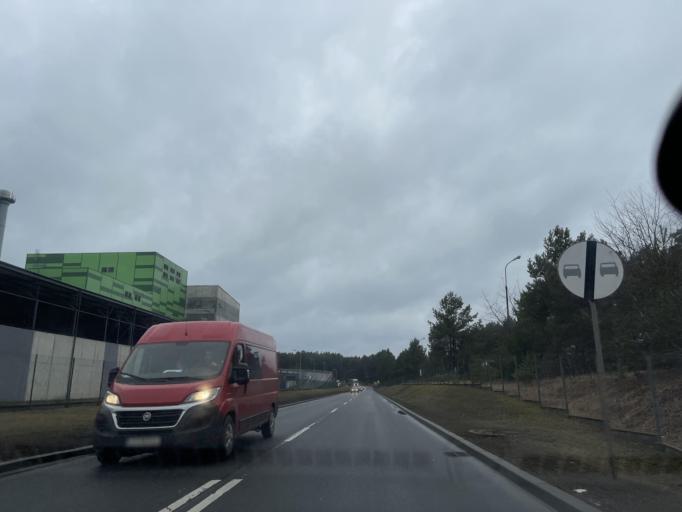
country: PL
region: Kujawsko-Pomorskie
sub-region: Bydgoszcz
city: Bydgoszcz
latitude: 53.0686
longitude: 18.0851
